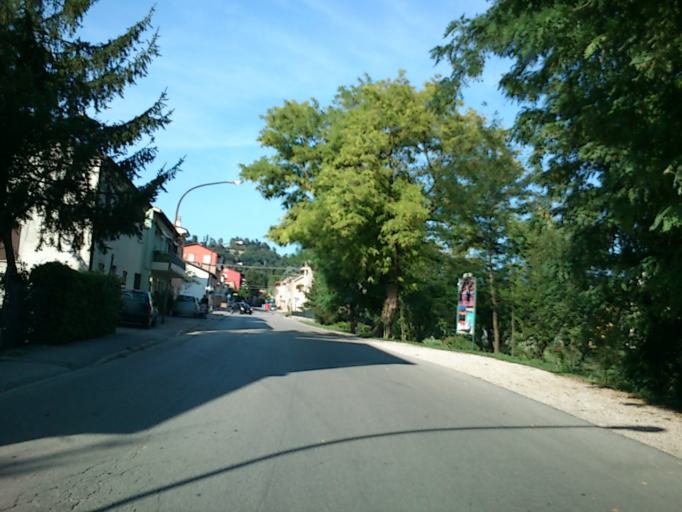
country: IT
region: The Marches
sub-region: Provincia di Pesaro e Urbino
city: Fermignano
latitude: 43.6909
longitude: 12.6433
